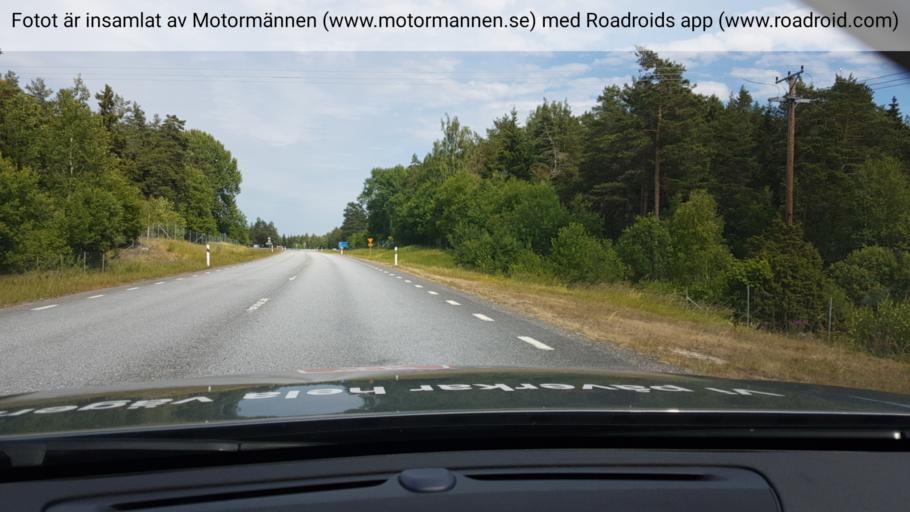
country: SE
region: Uppsala
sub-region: Osthammars Kommun
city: Anneberg
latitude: 60.1734
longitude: 18.3970
